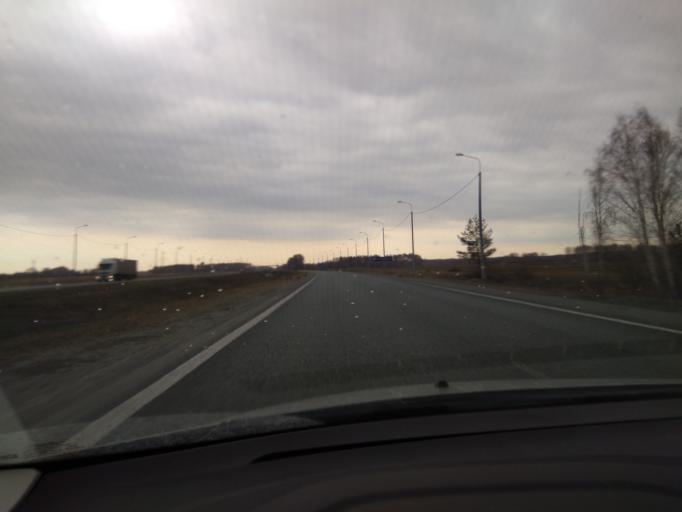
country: RU
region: Chelyabinsk
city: Kunashak
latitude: 55.7565
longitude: 61.2229
